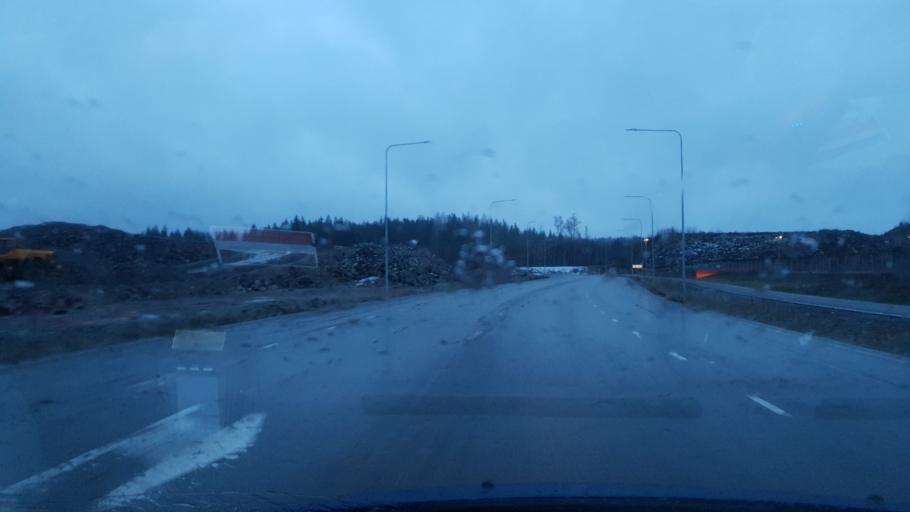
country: FI
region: Uusimaa
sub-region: Helsinki
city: Kerava
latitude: 60.3766
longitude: 25.1668
